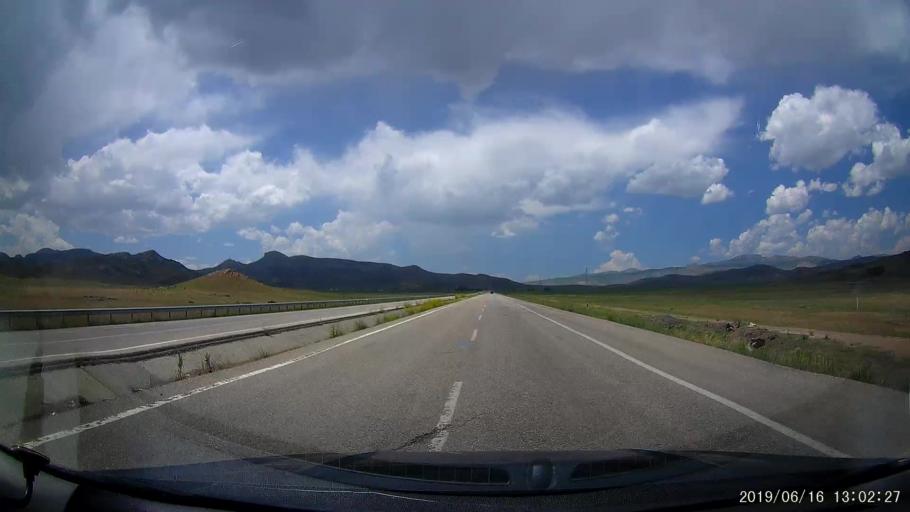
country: TR
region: Agri
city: Sulucem
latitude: 39.5746
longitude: 43.8160
